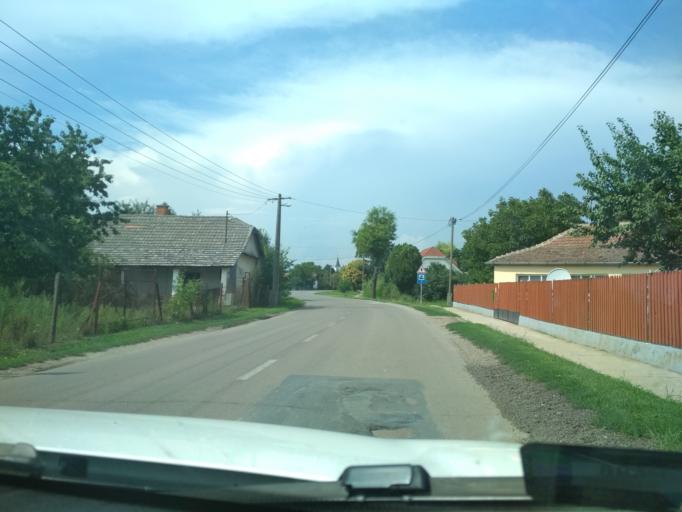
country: HU
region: Jasz-Nagykun-Szolnok
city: Tiszaszolos
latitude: 47.5539
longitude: 20.7198
